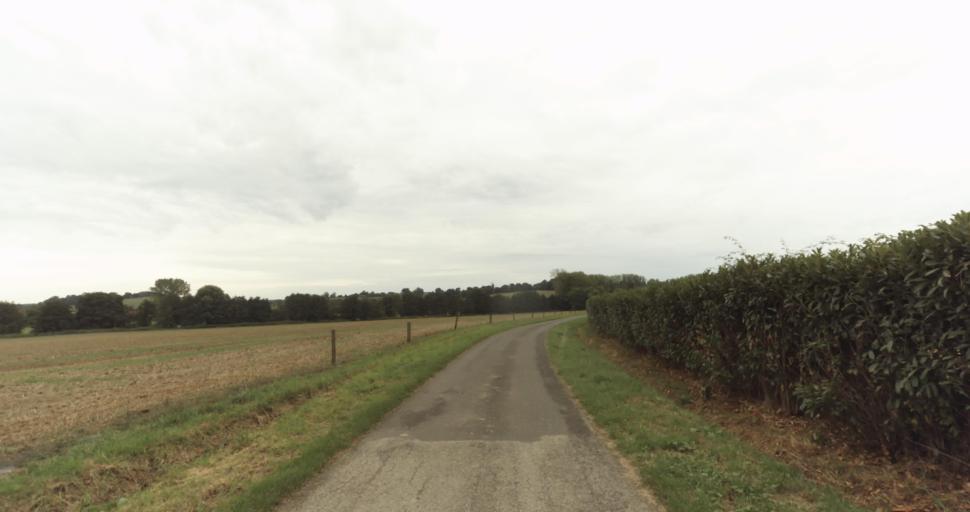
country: FR
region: Lower Normandy
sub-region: Departement de l'Orne
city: Sees
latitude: 48.6686
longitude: 0.2605
